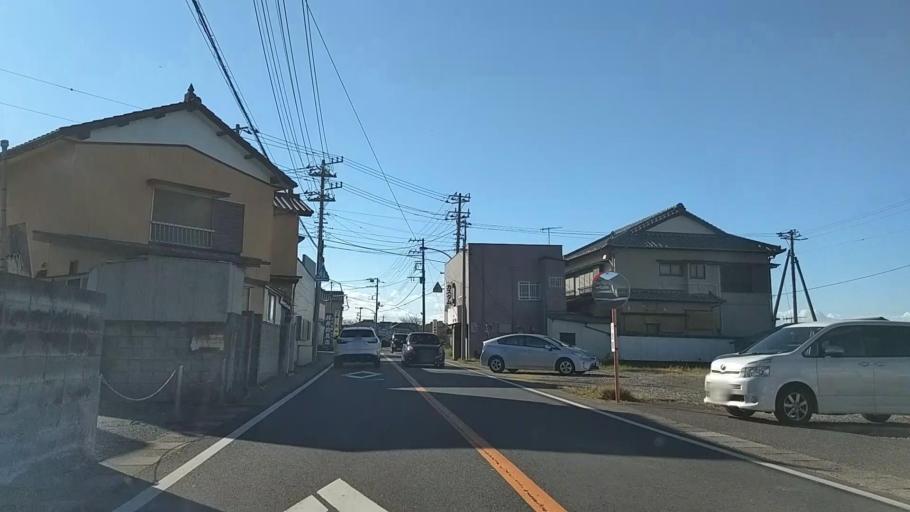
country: JP
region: Chiba
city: Tateyama
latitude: 35.1364
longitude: 139.8383
